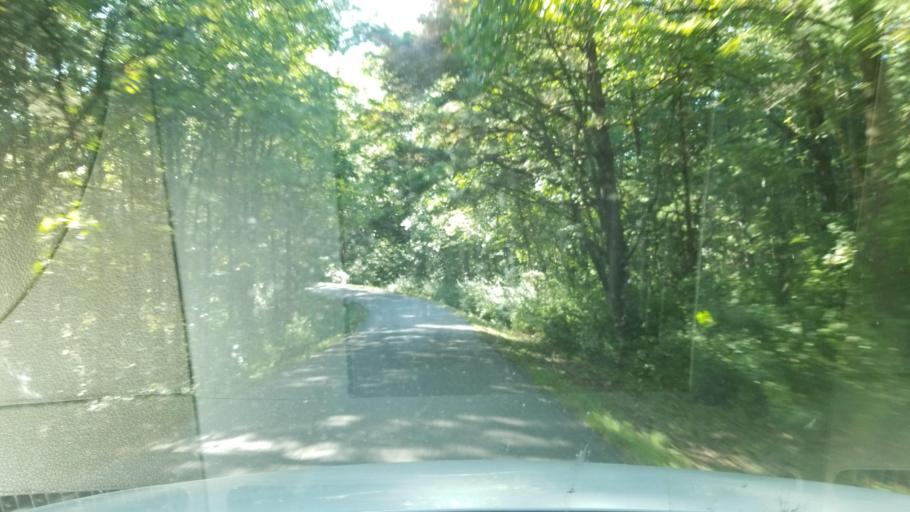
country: US
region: Illinois
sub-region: Hardin County
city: Elizabethtown
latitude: 37.6014
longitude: -88.3742
